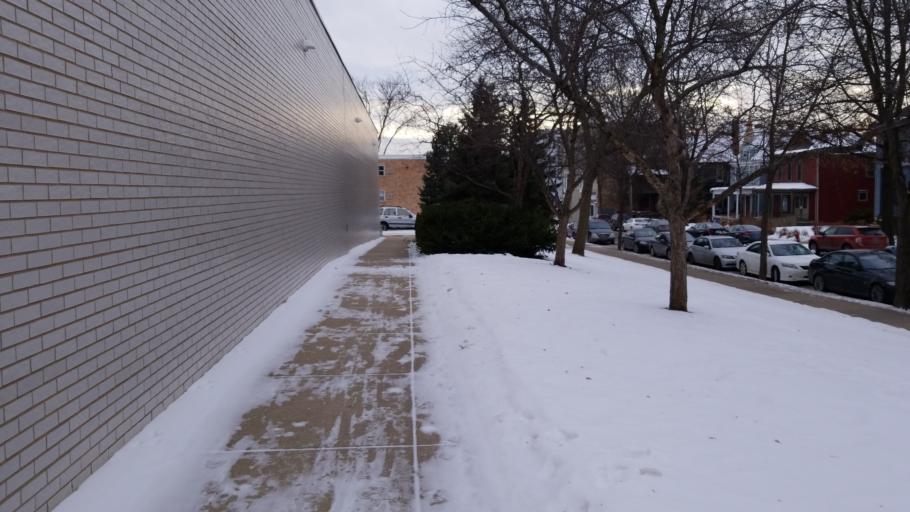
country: US
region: Minnesota
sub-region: Hennepin County
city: Minneapolis
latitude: 44.9568
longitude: -93.2751
